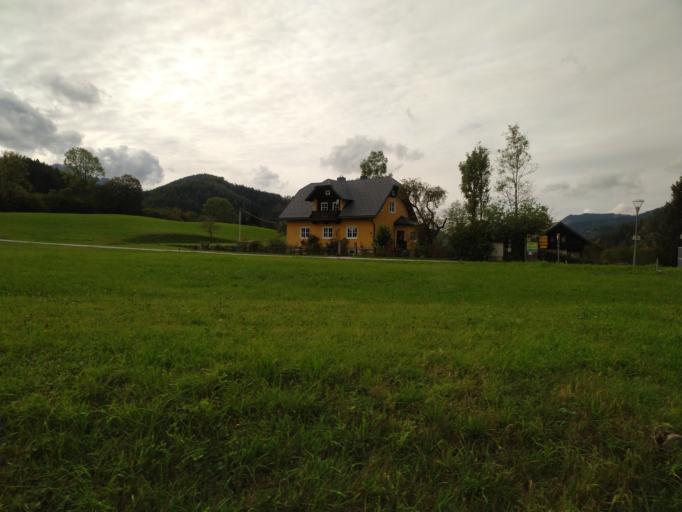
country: AT
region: Lower Austria
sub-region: Politischer Bezirk Lilienfeld
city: Mitterbach am Erlaufsee
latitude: 47.8643
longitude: 15.3107
